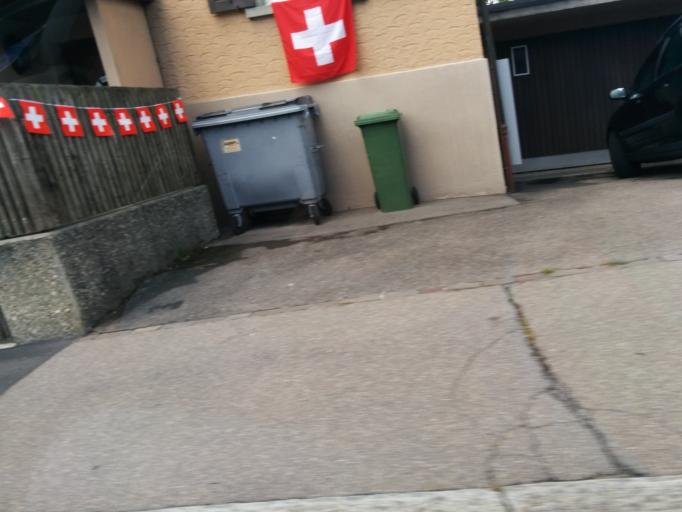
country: CH
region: Zurich
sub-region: Bezirk Meilen
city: Kuesnacht / Heslibach
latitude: 47.3150
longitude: 8.5925
